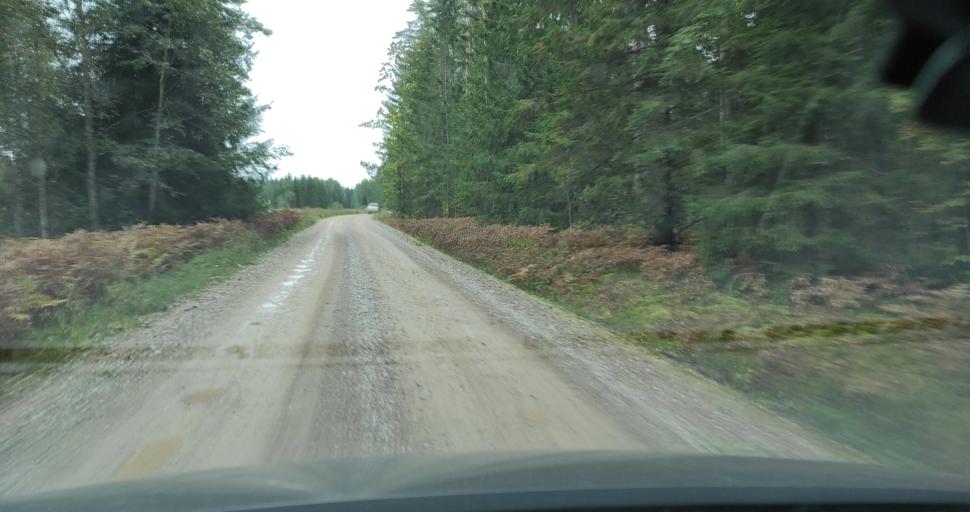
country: LV
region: Talsu Rajons
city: Stende
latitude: 57.0246
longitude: 22.3475
